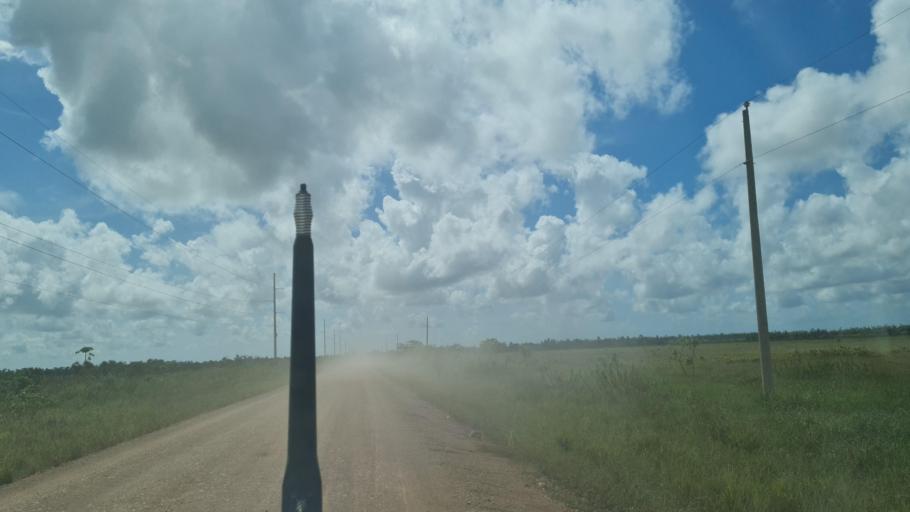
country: NI
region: Atlantico Norte (RAAN)
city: Puerto Cabezas
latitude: 14.1093
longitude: -83.5888
